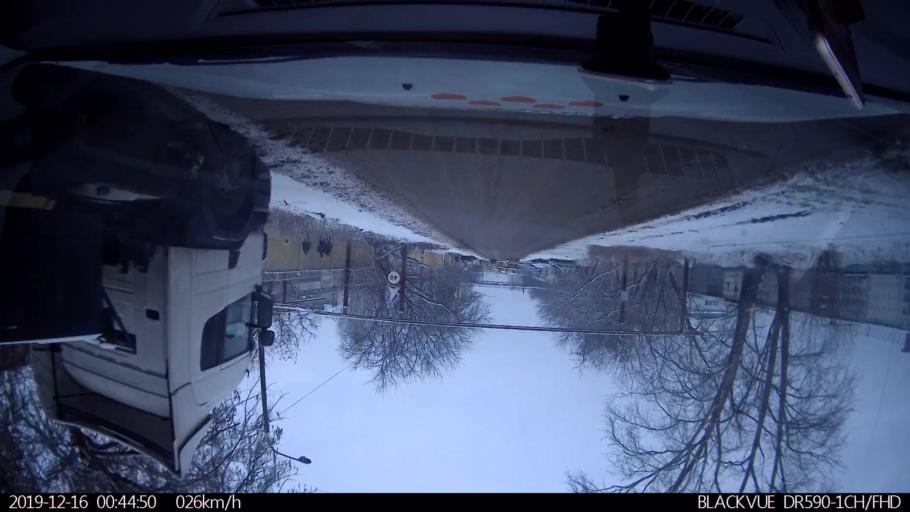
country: RU
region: Nizjnij Novgorod
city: Gorbatovka
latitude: 56.3021
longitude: 43.8606
